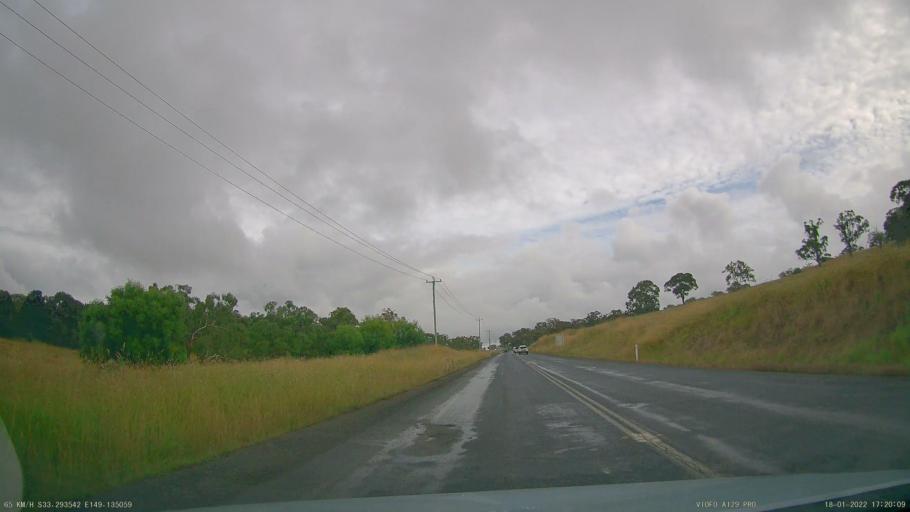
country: AU
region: New South Wales
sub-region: Orange Municipality
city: Orange
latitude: -33.2938
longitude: 149.1351
